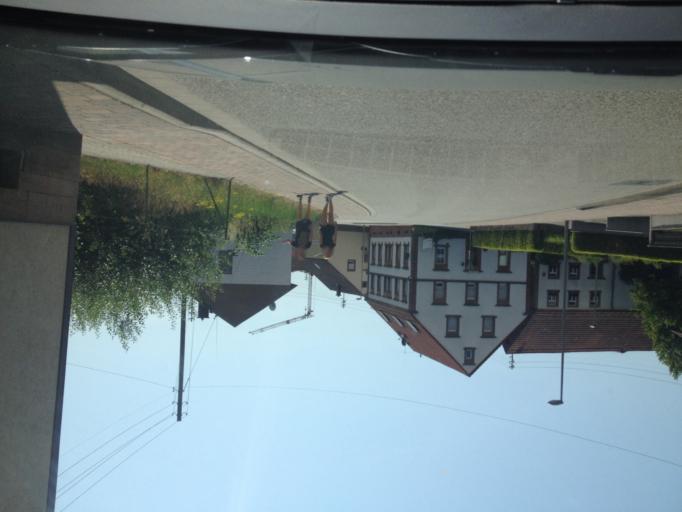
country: DE
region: Rheinland-Pfalz
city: Bruchmuhlbach-Miesau
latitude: 49.4077
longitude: 7.4310
